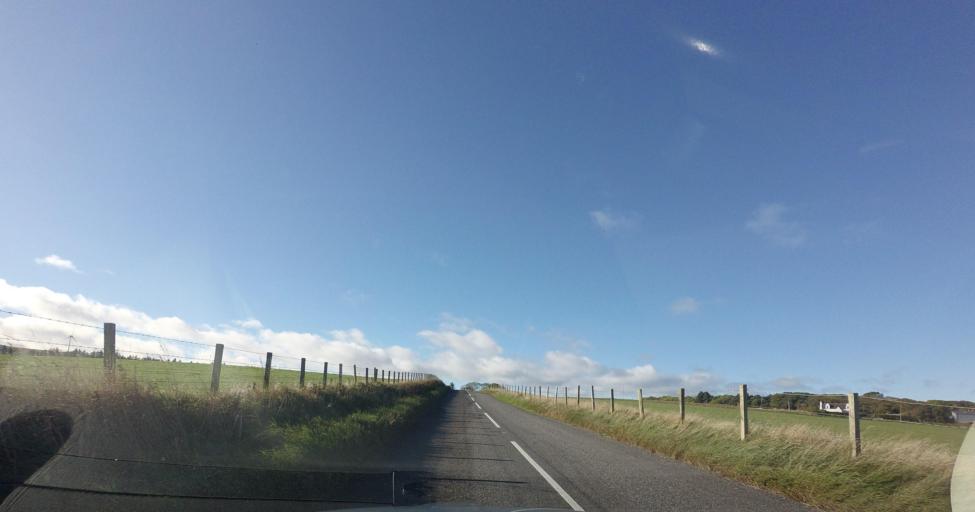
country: GB
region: Scotland
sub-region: Aberdeenshire
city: Rosehearty
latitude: 57.6793
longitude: -2.2789
